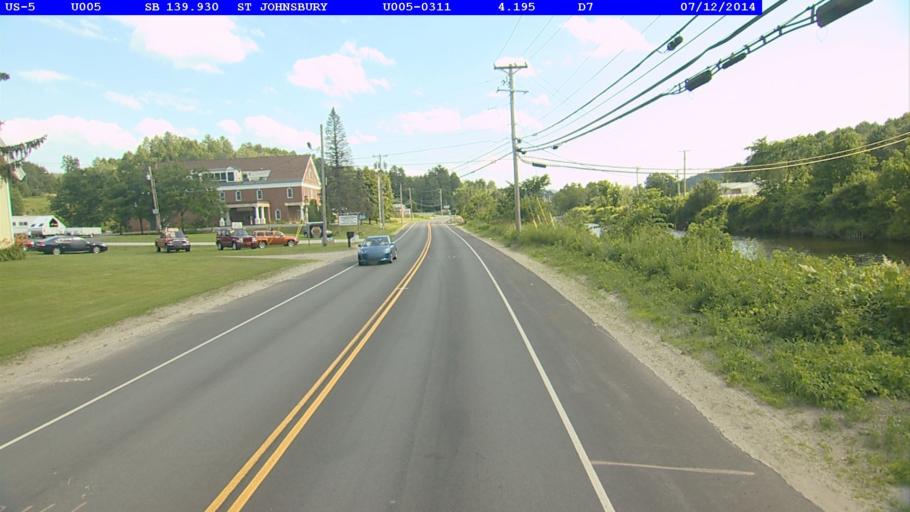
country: US
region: Vermont
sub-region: Caledonia County
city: St Johnsbury
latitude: 44.4517
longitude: -72.0162
